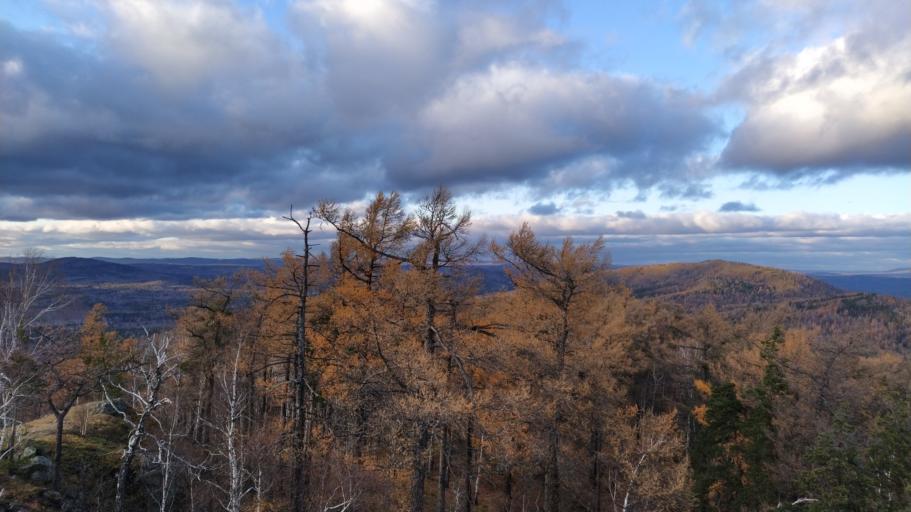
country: RU
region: Chelyabinsk
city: Kyshtym
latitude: 55.7254
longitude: 60.4408
